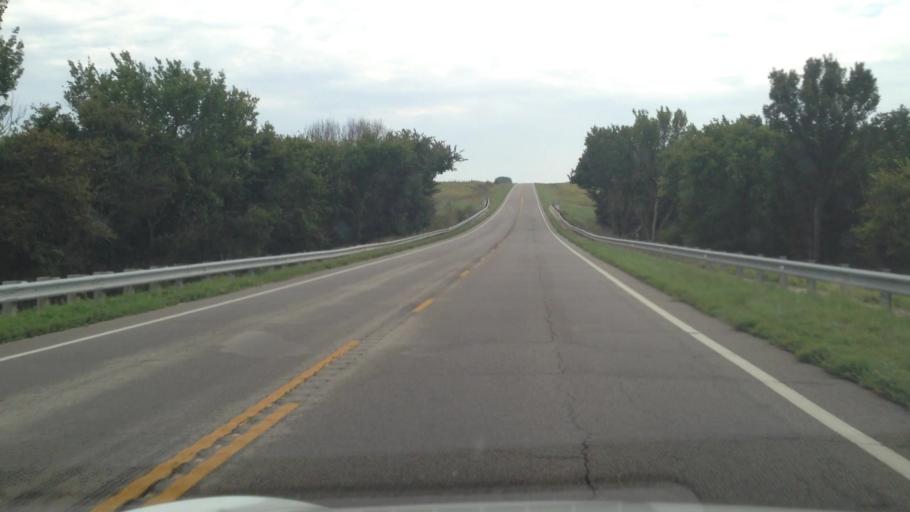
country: US
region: Kansas
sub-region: Bourbon County
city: Fort Scott
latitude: 37.8867
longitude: -95.0264
